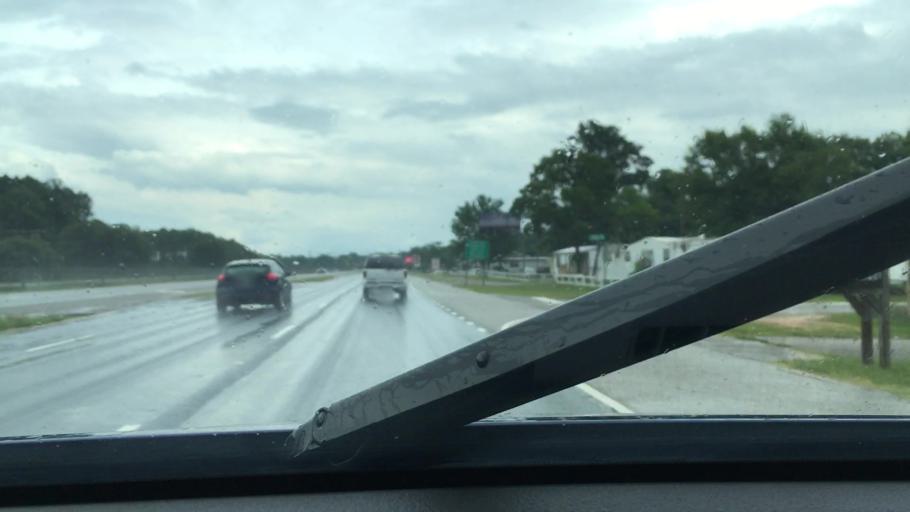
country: US
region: South Carolina
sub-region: Sumter County
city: Cherryvale
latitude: 33.9646
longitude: -80.4502
